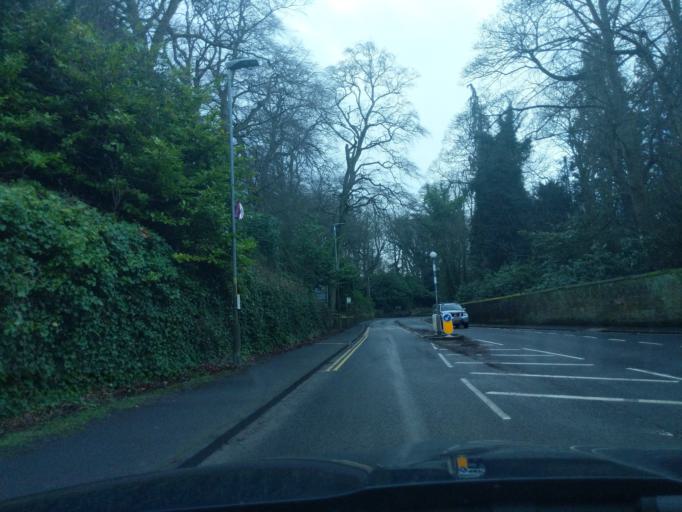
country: GB
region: England
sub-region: Northumberland
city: Alnwick
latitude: 55.4127
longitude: -1.6974
